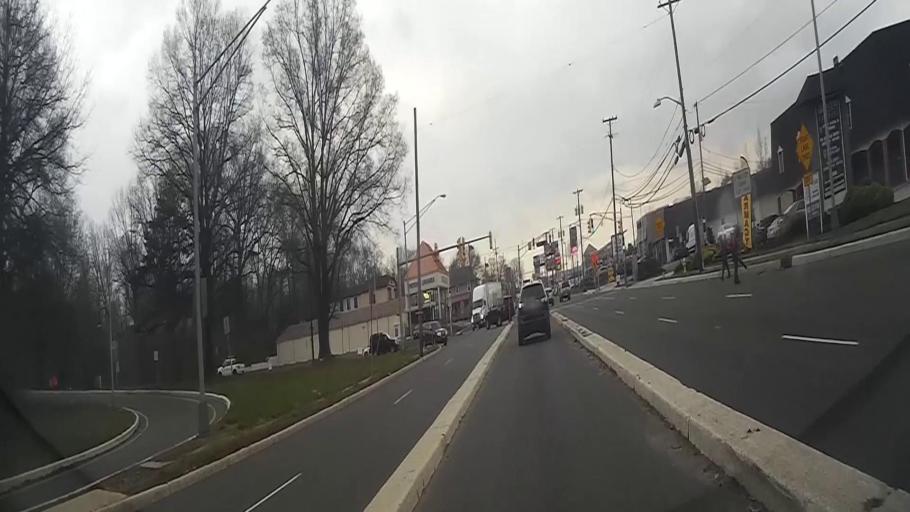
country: US
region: New Jersey
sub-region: Camden County
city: Barrington
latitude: 39.8739
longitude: -75.0470
